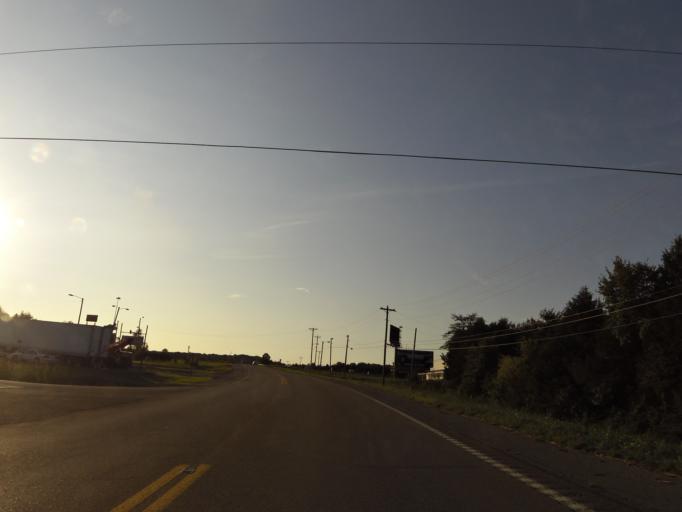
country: US
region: Tennessee
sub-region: McMinn County
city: Athens
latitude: 35.5016
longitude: -84.6075
